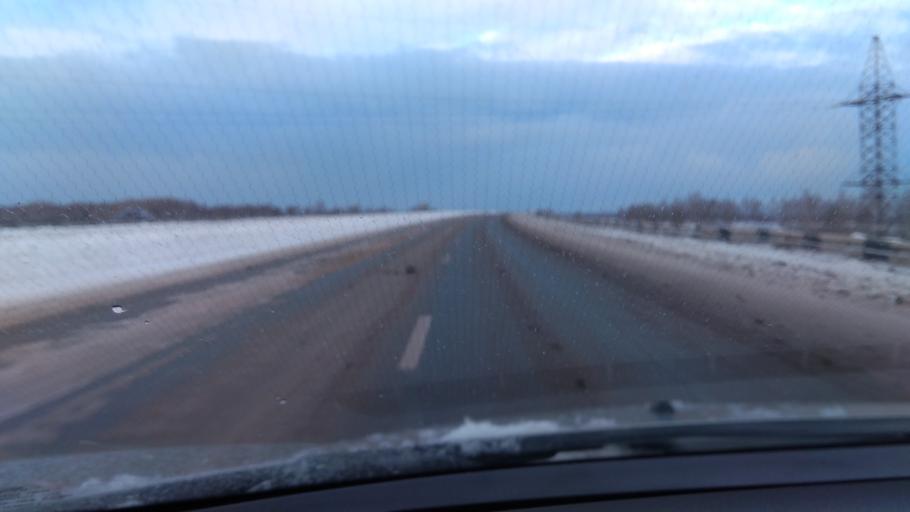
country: RU
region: Sverdlovsk
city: Tsementnyy
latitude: 57.5015
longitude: 60.1737
